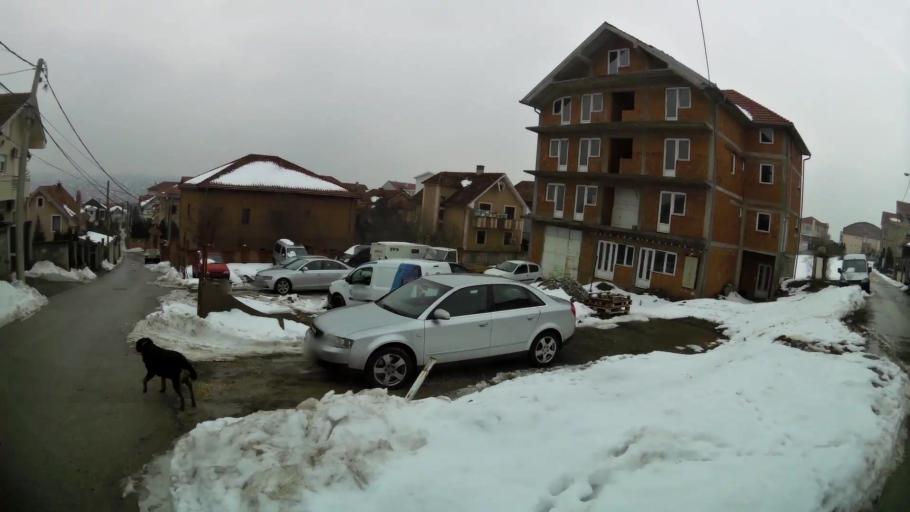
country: RS
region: Central Serbia
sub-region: Belgrade
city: Zvezdara
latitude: 44.7682
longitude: 20.5089
